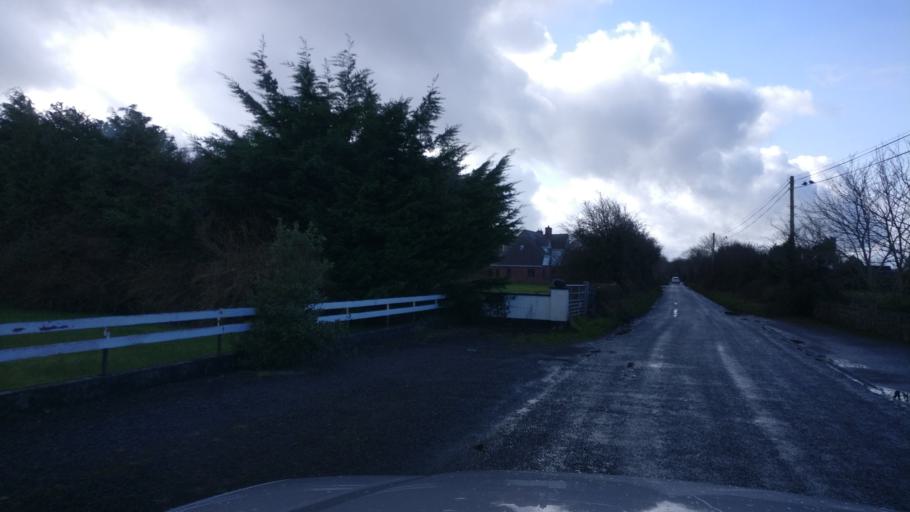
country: IE
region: Connaught
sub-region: County Galway
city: Oranmore
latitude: 53.2481
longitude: -8.9085
